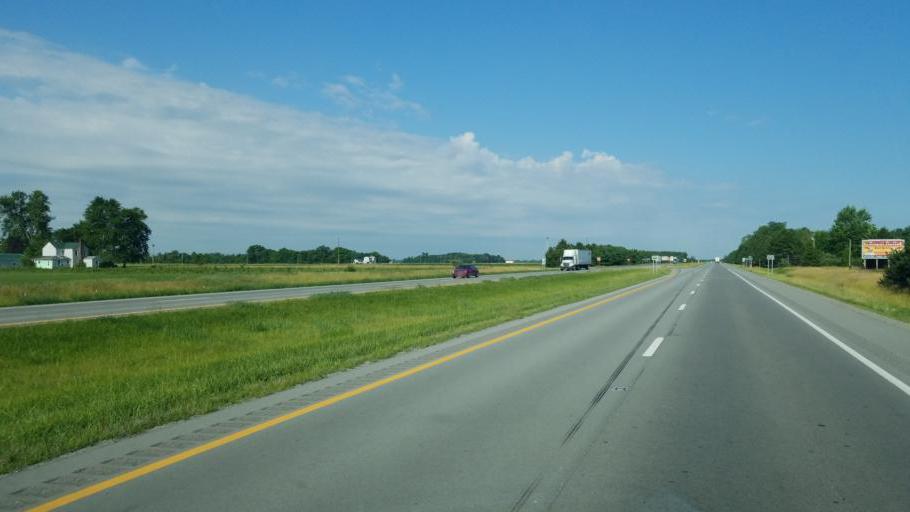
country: US
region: Ohio
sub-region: Hancock County
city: Findlay
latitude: 40.9860
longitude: -83.5911
